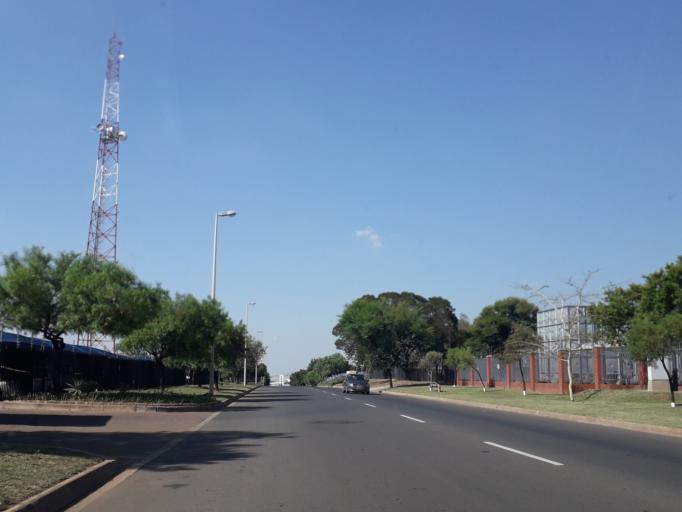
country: ZA
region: Gauteng
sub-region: City of Johannesburg Metropolitan Municipality
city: Midrand
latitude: -25.9393
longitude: 28.1437
